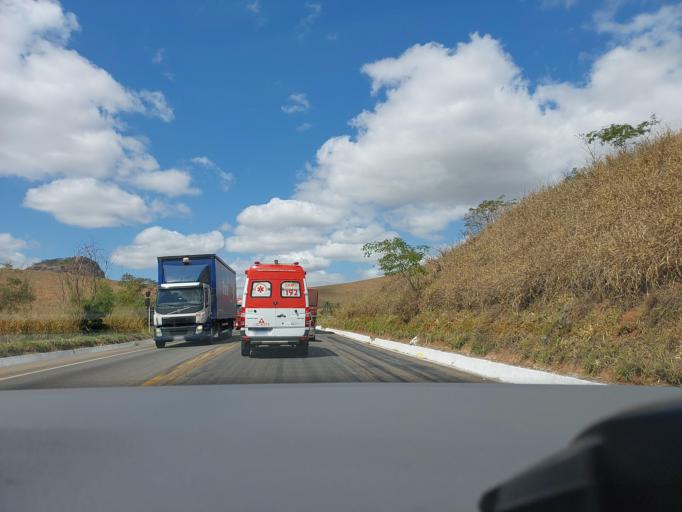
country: BR
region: Minas Gerais
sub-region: Muriae
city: Muriae
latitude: -21.1263
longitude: -42.3276
